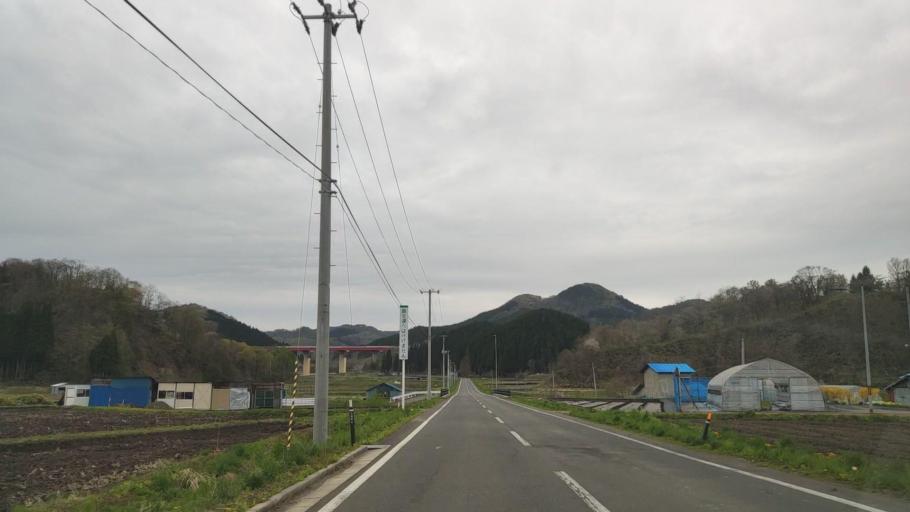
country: JP
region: Akita
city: Odate
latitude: 40.3710
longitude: 140.7258
